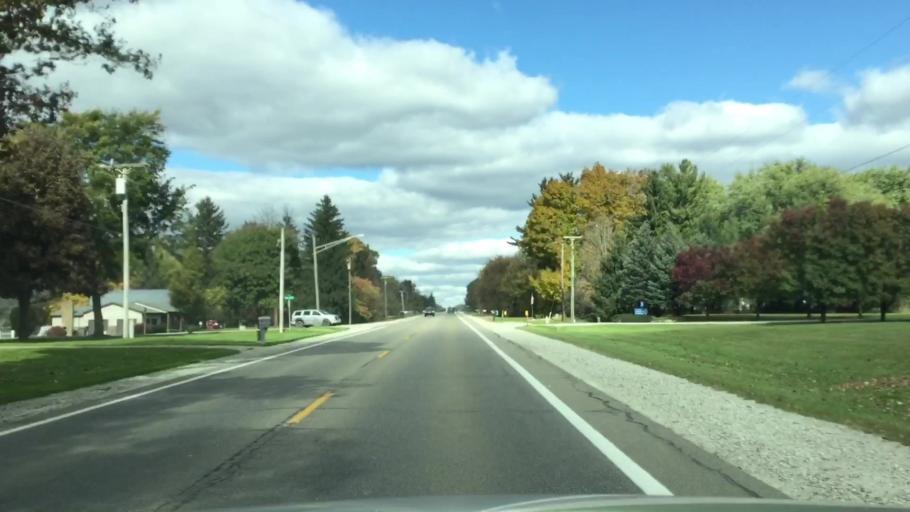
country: US
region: Michigan
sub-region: Lapeer County
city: Lapeer
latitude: 43.1102
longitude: -83.3088
